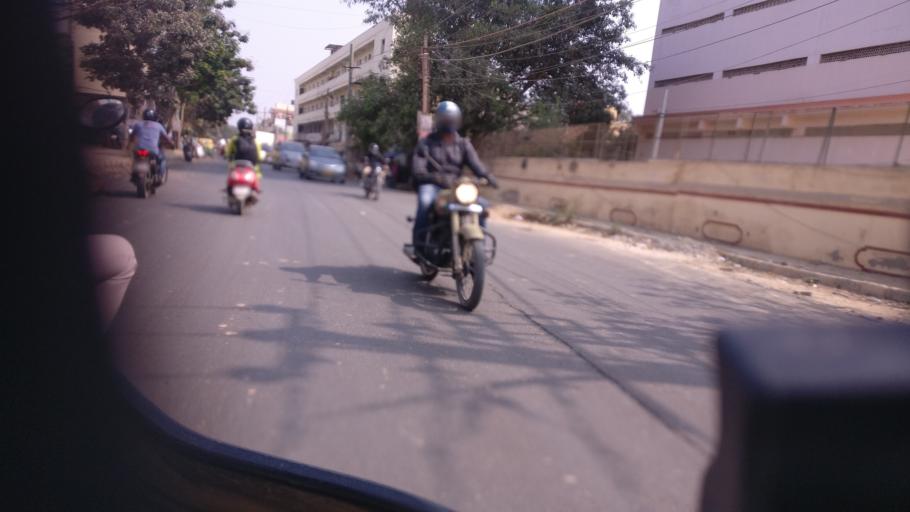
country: IN
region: Karnataka
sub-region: Bangalore Urban
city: Bangalore
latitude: 12.8976
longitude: 77.6753
